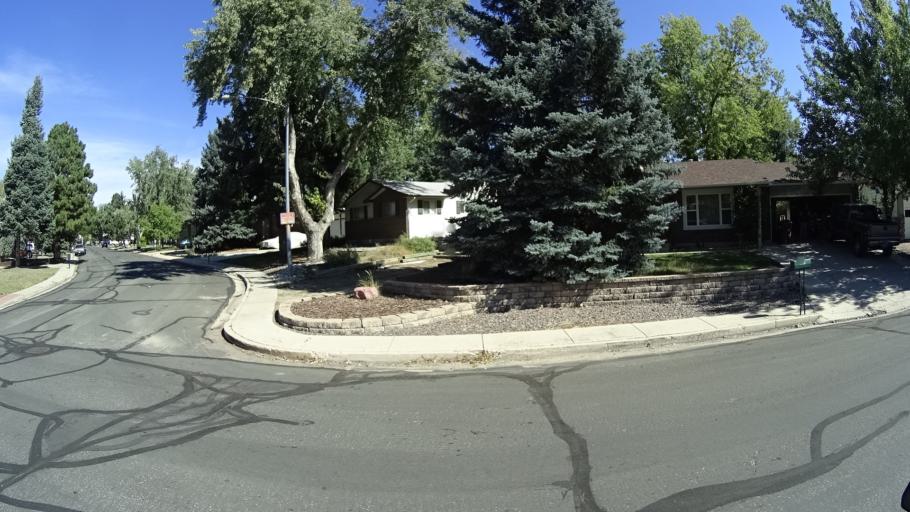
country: US
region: Colorado
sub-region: El Paso County
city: Cimarron Hills
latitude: 38.9016
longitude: -104.7627
